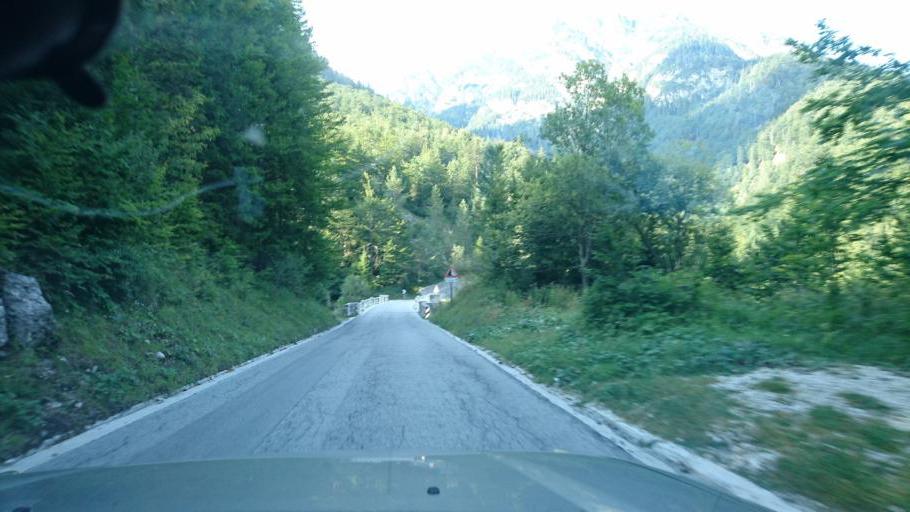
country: SI
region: Bovec
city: Bovec
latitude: 46.4080
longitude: 13.5336
